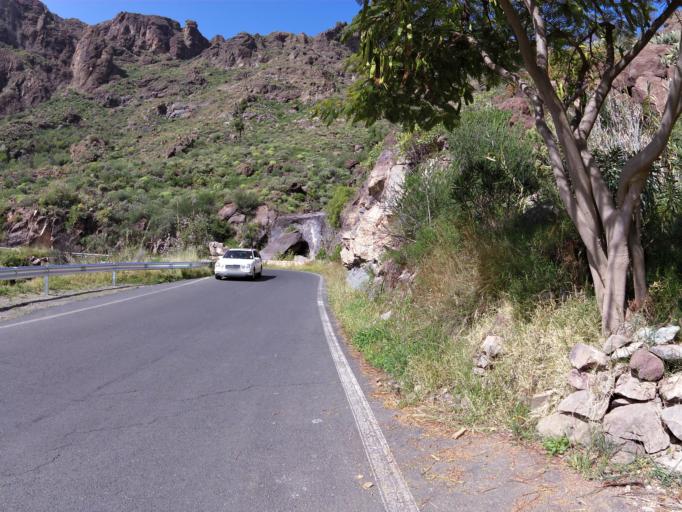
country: ES
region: Canary Islands
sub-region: Provincia de Las Palmas
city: Mogan
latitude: 27.9040
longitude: -15.6745
